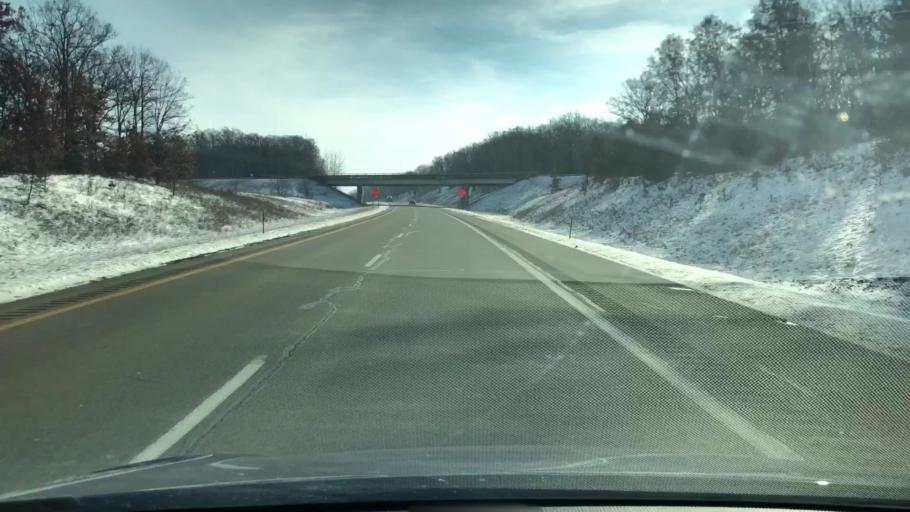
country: US
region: Michigan
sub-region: Roscommon County
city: Roscommon
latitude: 44.4951
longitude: -84.6492
